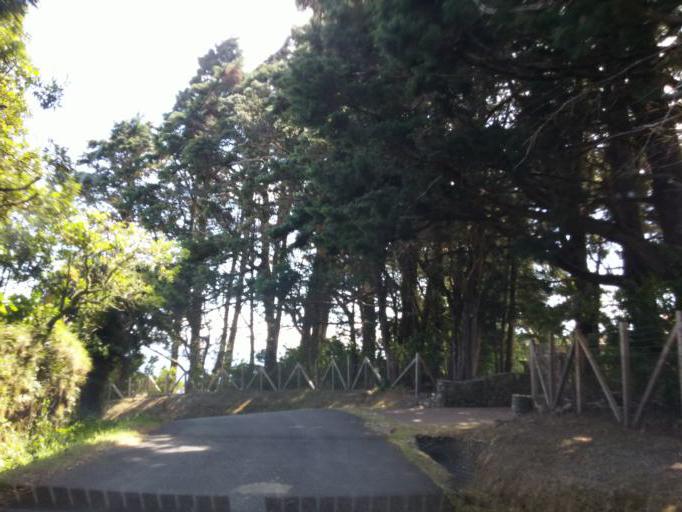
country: CR
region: Heredia
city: Santo Domingo
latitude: 10.1088
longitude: -84.1231
